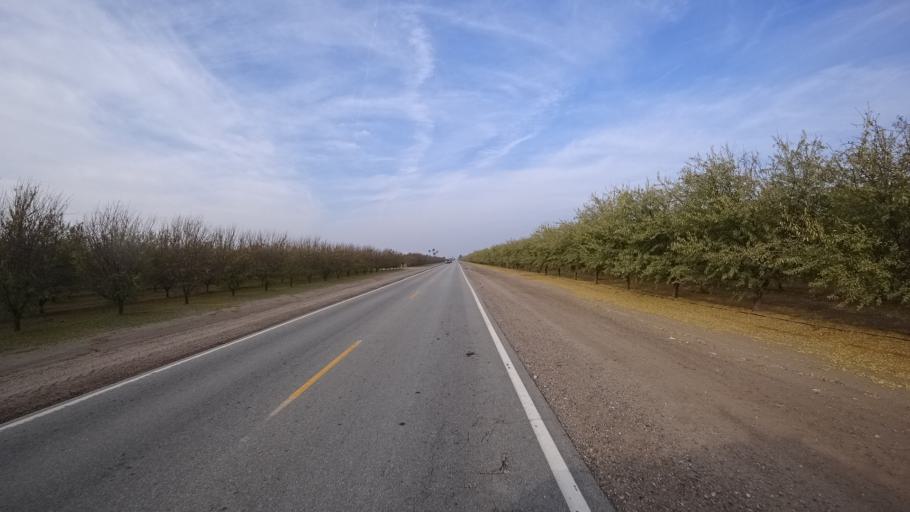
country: US
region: California
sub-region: Kern County
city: Greenacres
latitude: 35.2732
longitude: -119.1283
